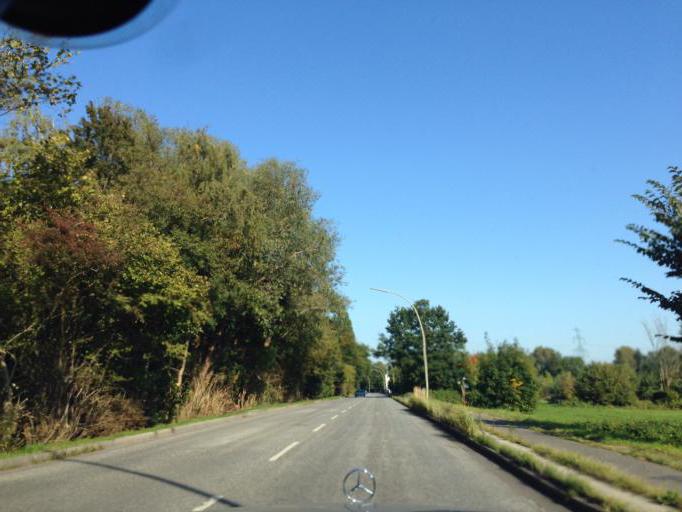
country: DE
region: Schleswig-Holstein
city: Stapelfeld
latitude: 53.6286
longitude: 10.1774
